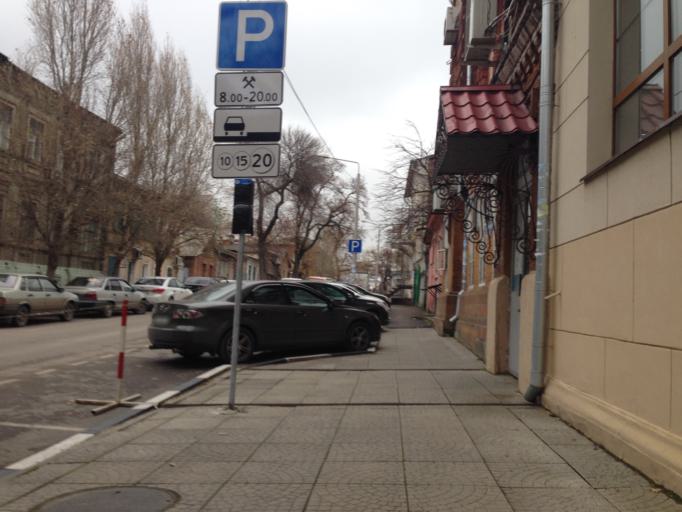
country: RU
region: Rostov
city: Rostov-na-Donu
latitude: 47.2176
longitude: 39.7179
